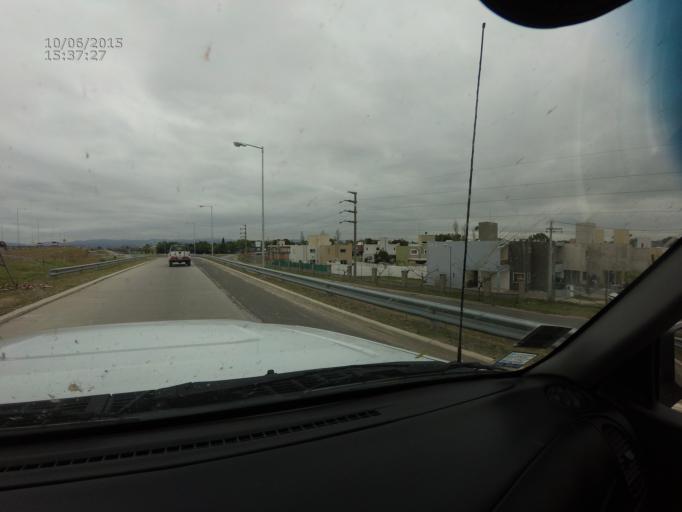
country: AR
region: Cordoba
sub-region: Departamento de Capital
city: Cordoba
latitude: -31.3535
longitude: -64.2225
